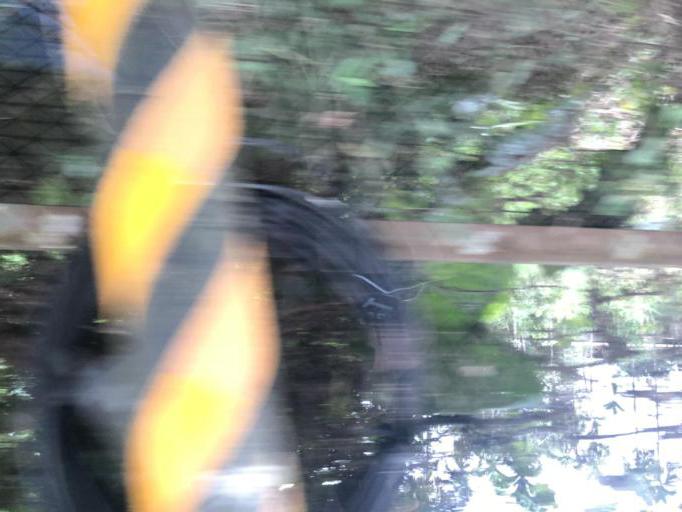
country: TW
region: Taiwan
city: Daxi
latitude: 24.9146
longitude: 121.3630
